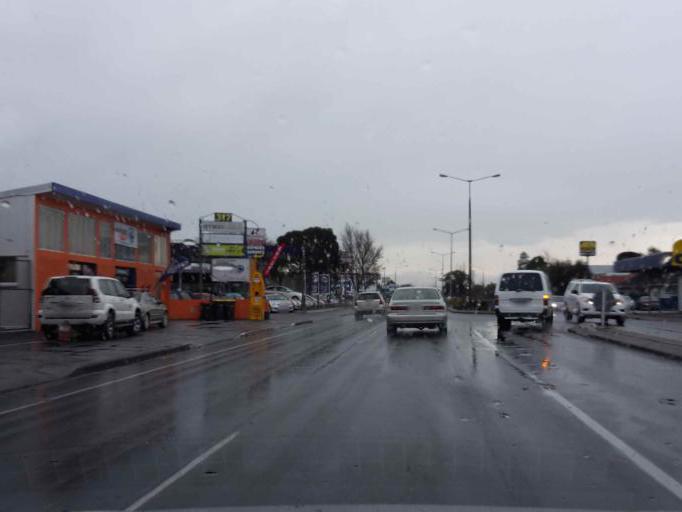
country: NZ
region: Canterbury
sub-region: Christchurch City
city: Christchurch
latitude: -43.5387
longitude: 172.5815
